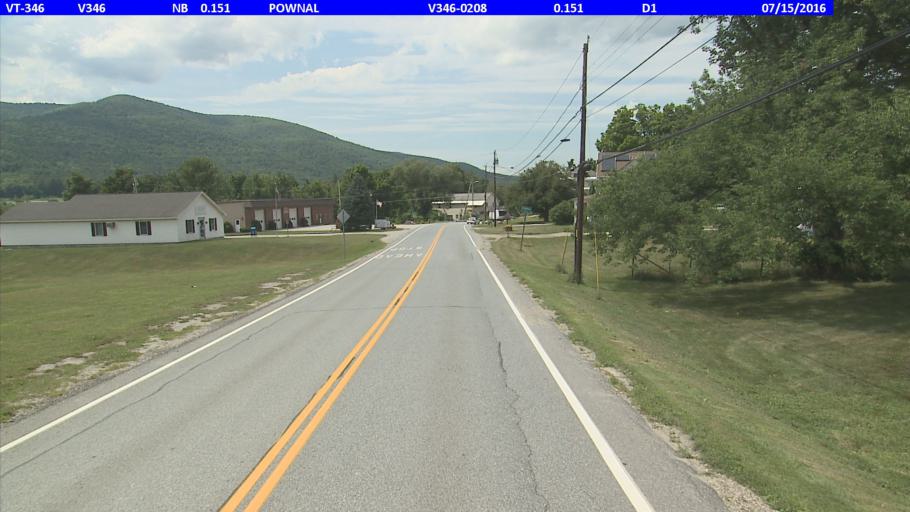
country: US
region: Massachusetts
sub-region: Berkshire County
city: Williamstown
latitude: 42.7646
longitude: -73.2346
